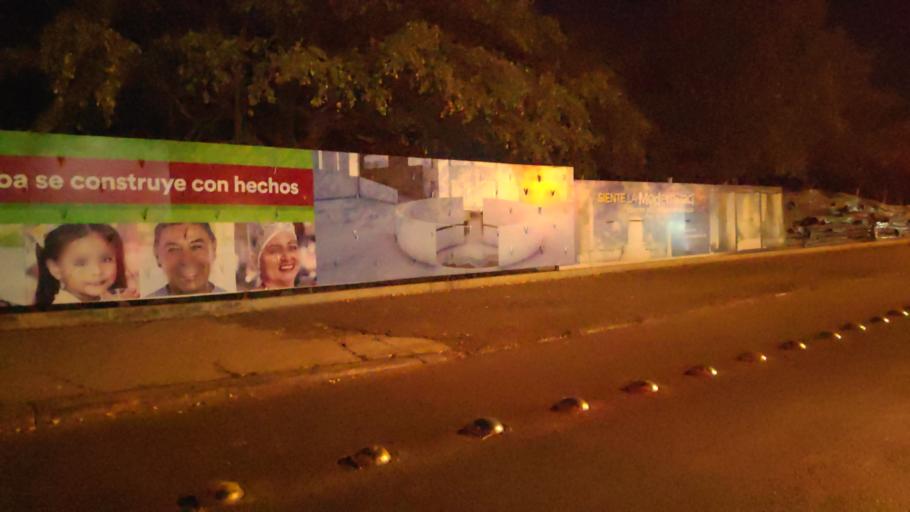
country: MX
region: Sinaloa
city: Culiacan
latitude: 24.8300
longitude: -107.3849
